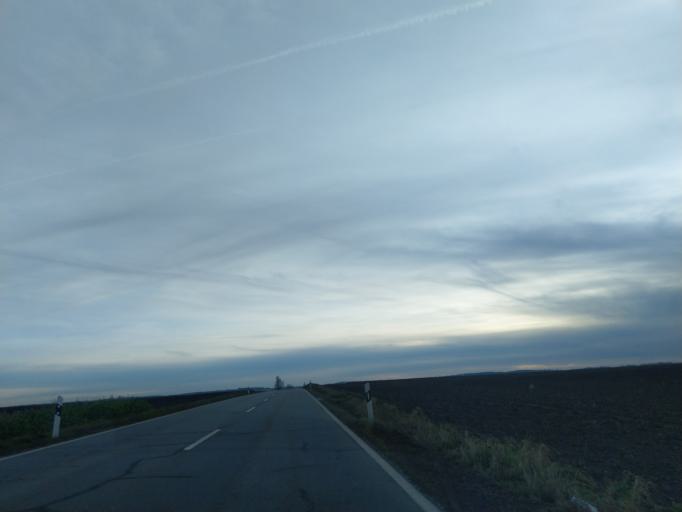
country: DE
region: Bavaria
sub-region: Lower Bavaria
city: Aholming
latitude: 48.7221
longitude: 12.8868
